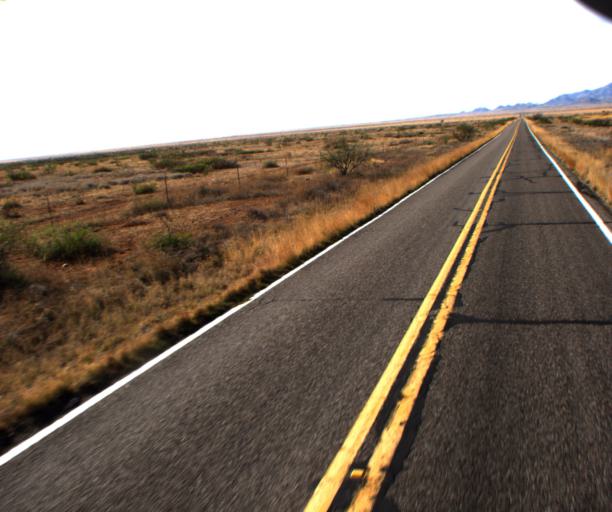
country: US
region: Arizona
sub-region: Cochise County
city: Willcox
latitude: 32.0539
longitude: -109.4948
